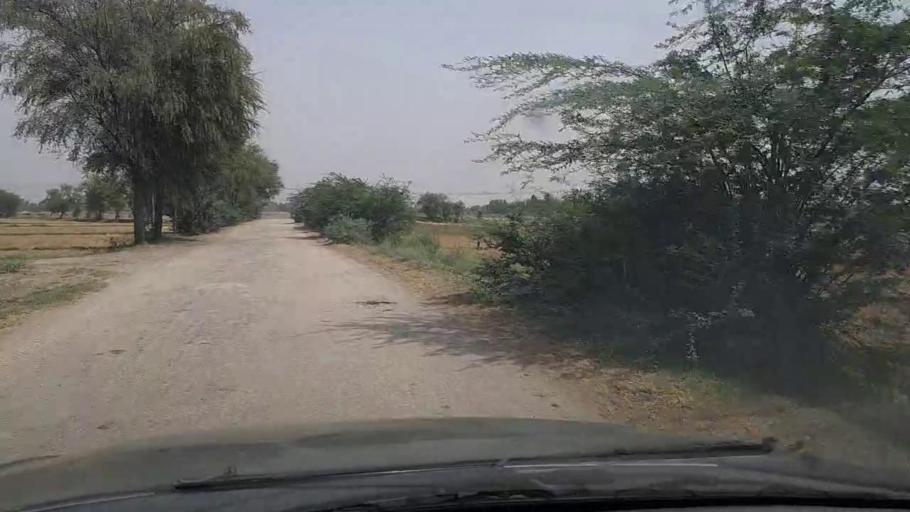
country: PK
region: Sindh
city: Shikarpur
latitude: 27.9176
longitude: 68.6837
